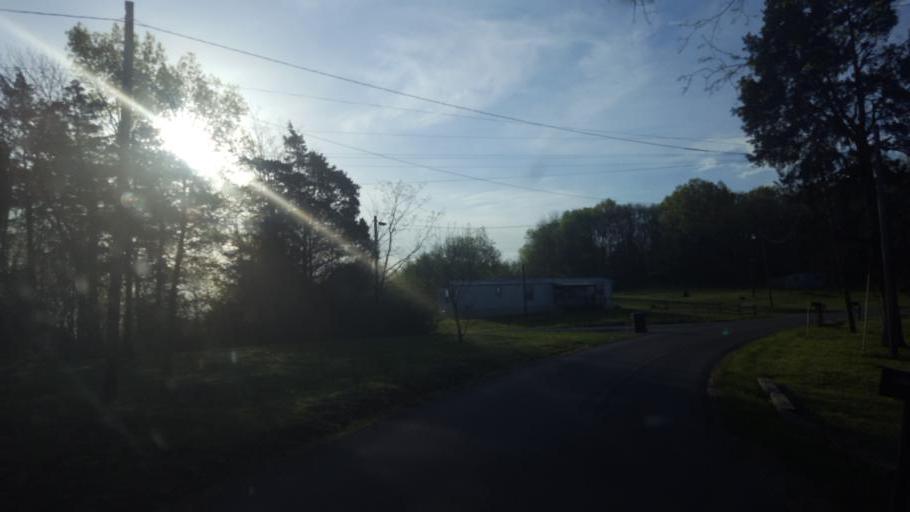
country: US
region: Kentucky
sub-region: Hart County
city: Munfordville
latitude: 37.2454
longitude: -85.8996
